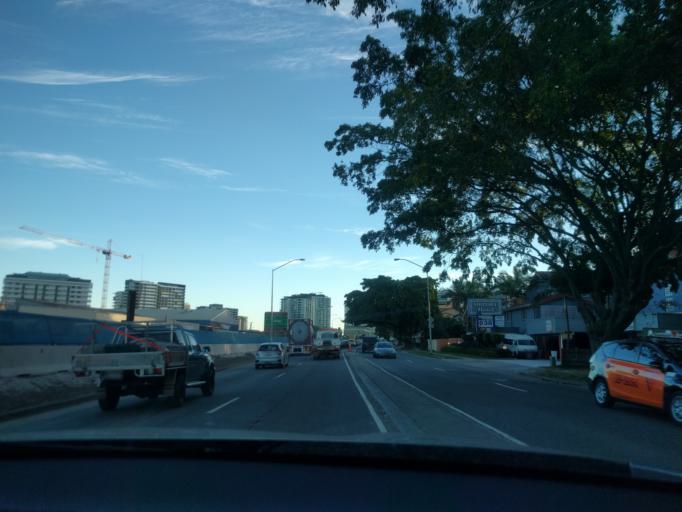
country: AU
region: Queensland
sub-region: Brisbane
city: Ascot
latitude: -27.4366
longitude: 153.0732
